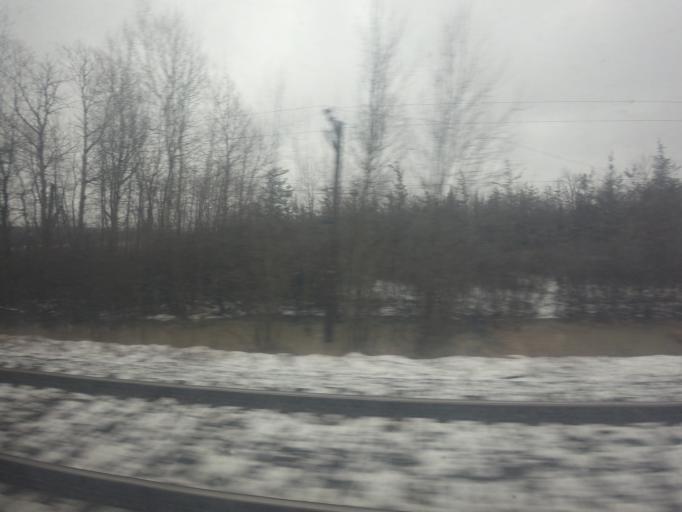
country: CA
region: Ontario
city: Belleville
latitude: 44.1522
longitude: -77.4737
